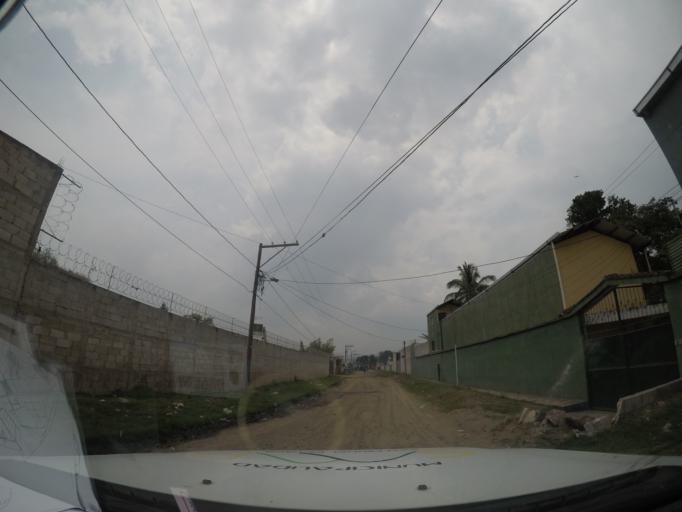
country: GT
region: Guatemala
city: Petapa
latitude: 14.5069
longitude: -90.5546
